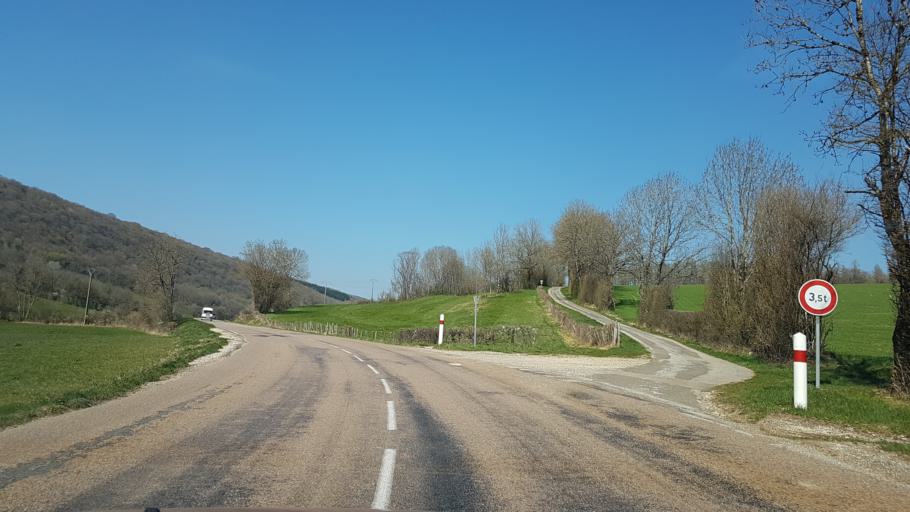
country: FR
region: Franche-Comte
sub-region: Departement du Jura
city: Orgelet
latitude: 46.5460
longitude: 5.6552
